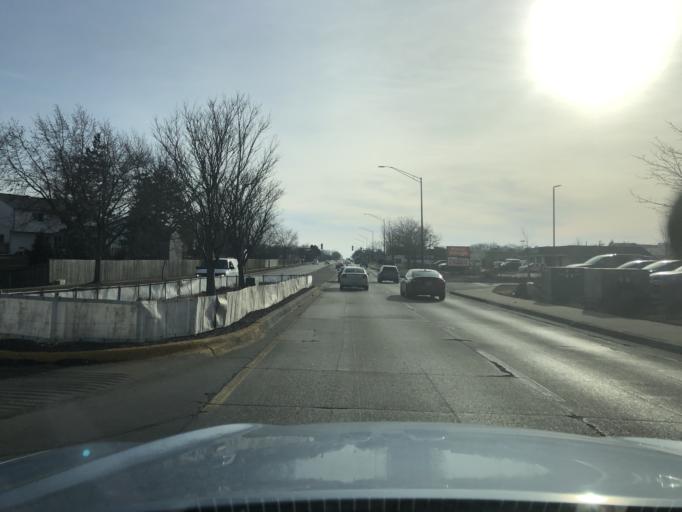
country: US
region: Illinois
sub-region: Cook County
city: Schaumburg
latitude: 42.0104
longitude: -88.0801
